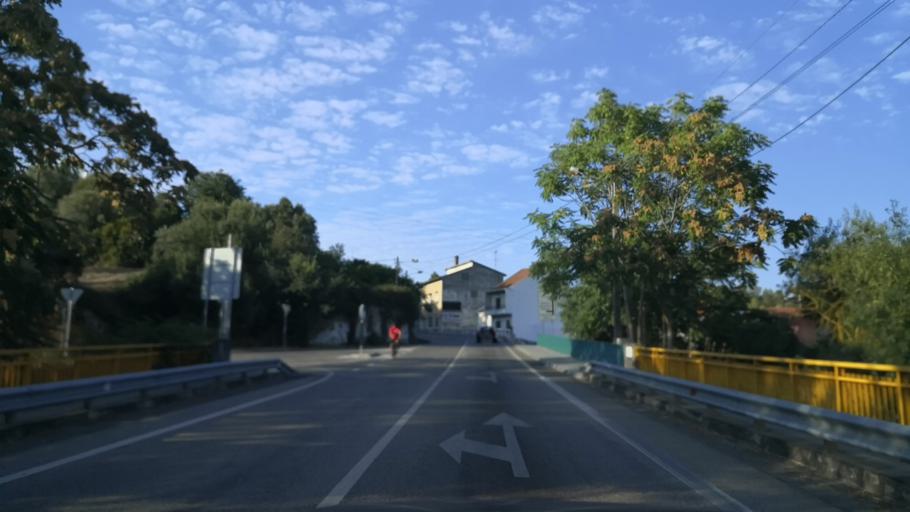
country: PT
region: Santarem
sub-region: Alcanena
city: Alcanena
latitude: 39.3815
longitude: -8.6605
